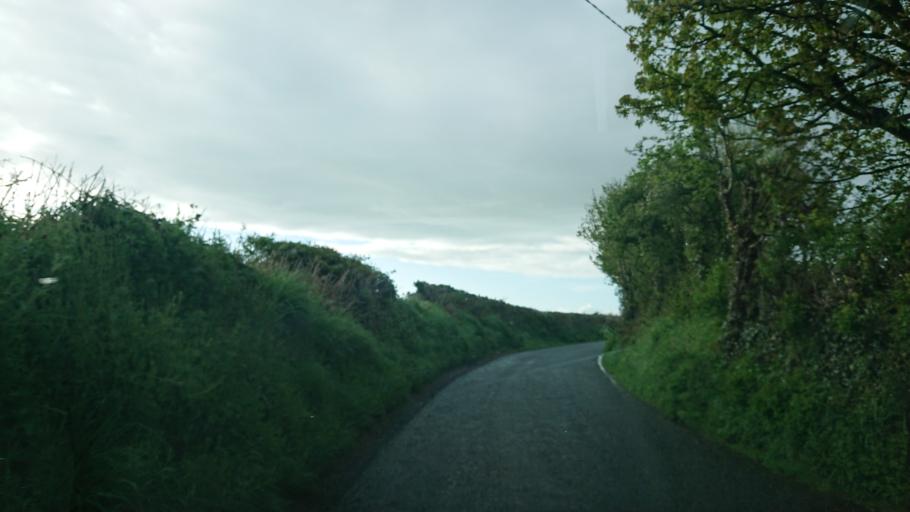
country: IE
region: Munster
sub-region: Waterford
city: Waterford
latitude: 52.2231
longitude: -7.1316
